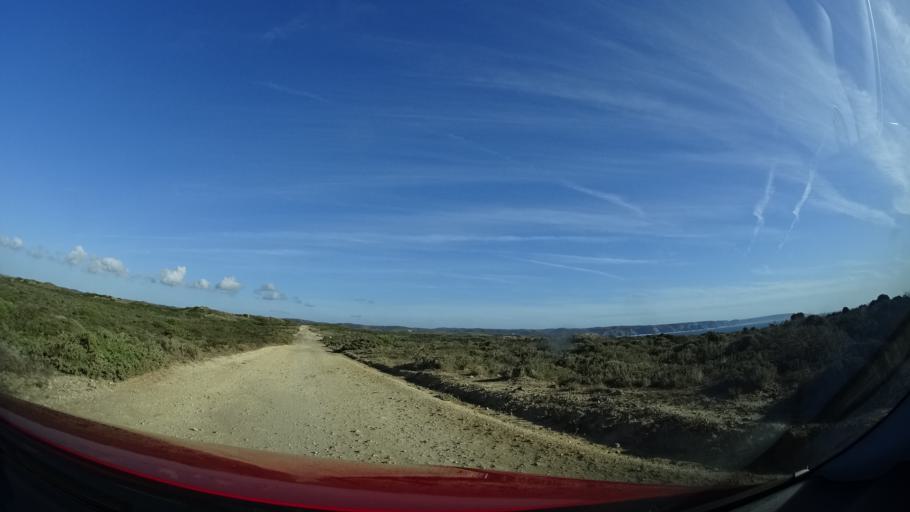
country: PT
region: Faro
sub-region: Vila do Bispo
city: Vila do Bispo
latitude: 37.1948
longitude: -8.9148
